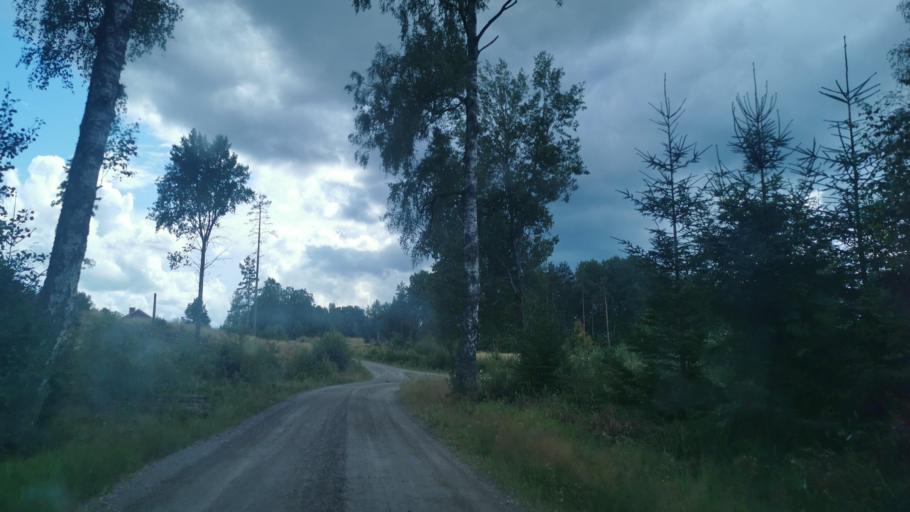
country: SE
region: OEstergoetland
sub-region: Finspangs Kommun
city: Finspang
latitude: 58.7940
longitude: 15.7724
